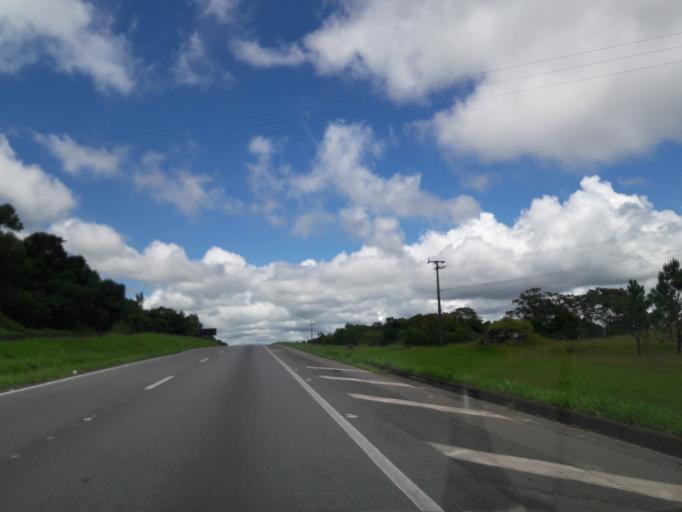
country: BR
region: Parana
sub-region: Campina Grande Do Sul
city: Campina Grande do Sul
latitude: -25.1421
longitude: -48.8567
